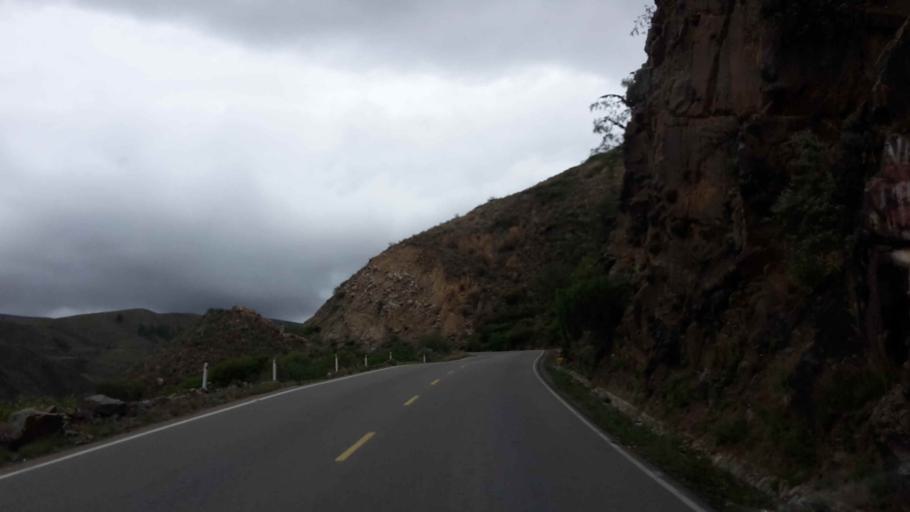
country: BO
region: Cochabamba
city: Punata
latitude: -17.4999
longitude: -65.7947
